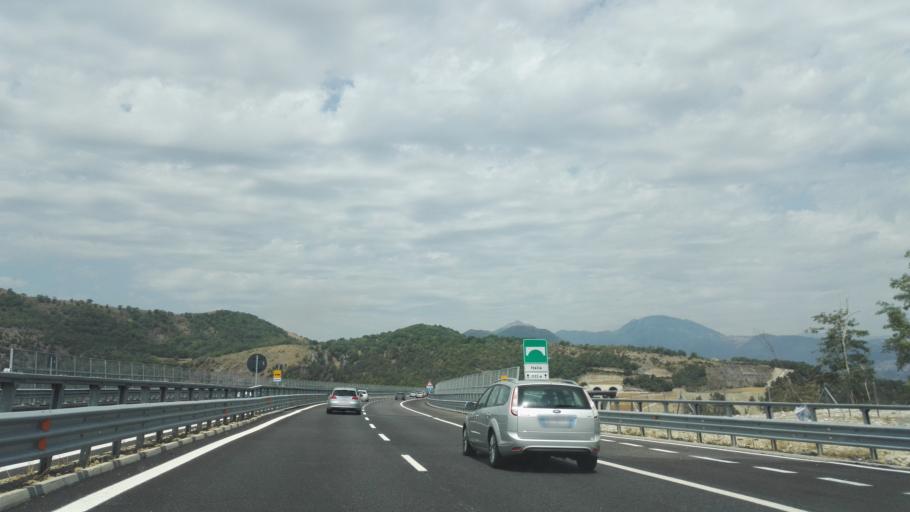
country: IT
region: Calabria
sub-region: Provincia di Cosenza
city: Laino Castello-Nuovo Centro
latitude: 39.9333
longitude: 15.9618
